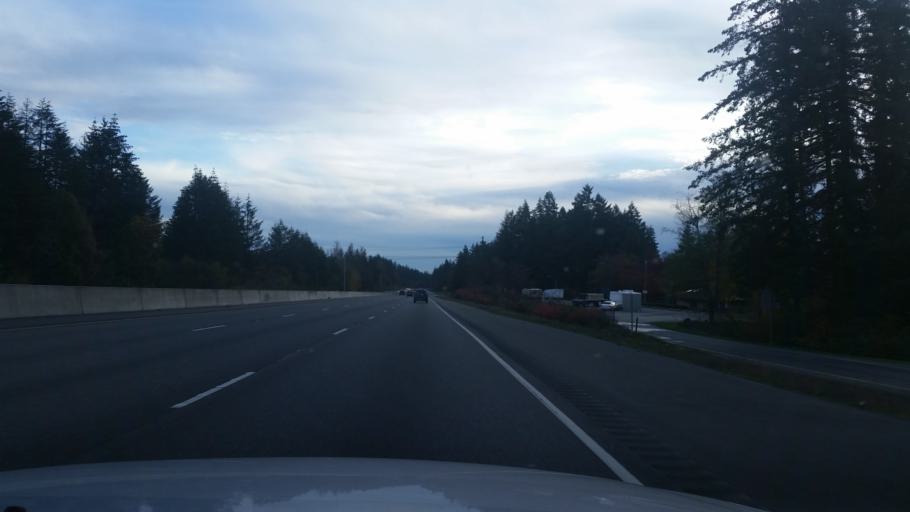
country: US
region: Washington
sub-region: Thurston County
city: Grand Mound
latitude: 46.8724
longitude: -122.9689
